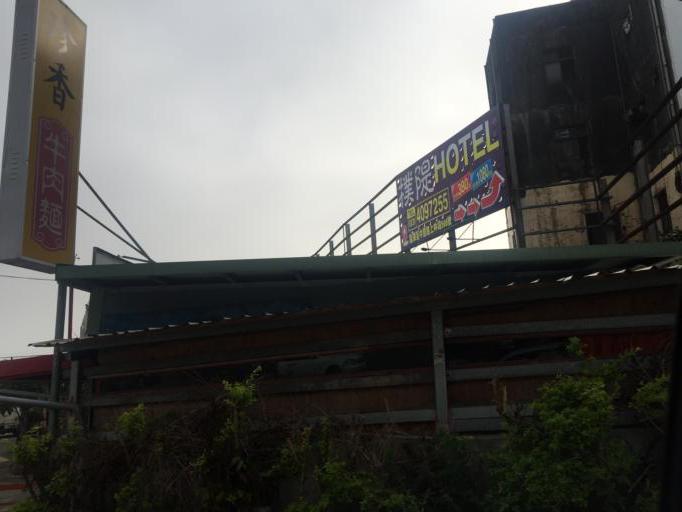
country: TW
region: Taiwan
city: Daxi
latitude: 24.8580
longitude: 121.2022
